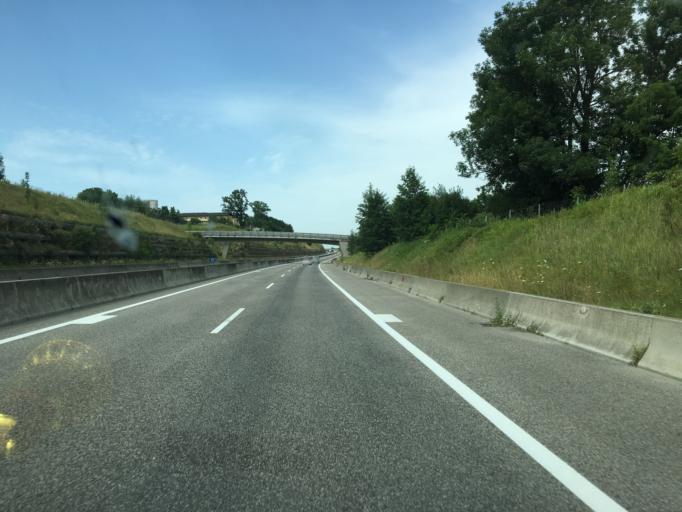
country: AT
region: Upper Austria
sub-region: Wels-Land
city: Steinhaus
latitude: 48.0860
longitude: 14.0198
